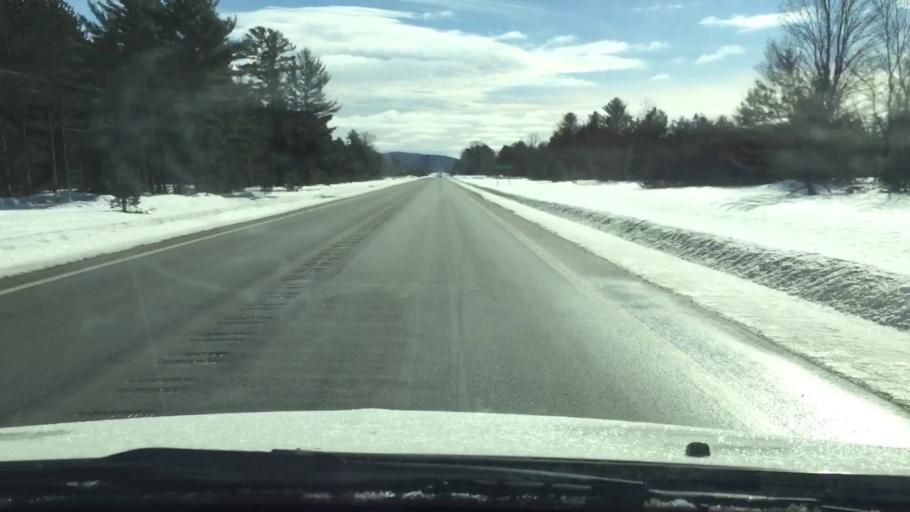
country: US
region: Michigan
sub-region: Antrim County
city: Mancelona
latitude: 44.9343
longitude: -85.0509
